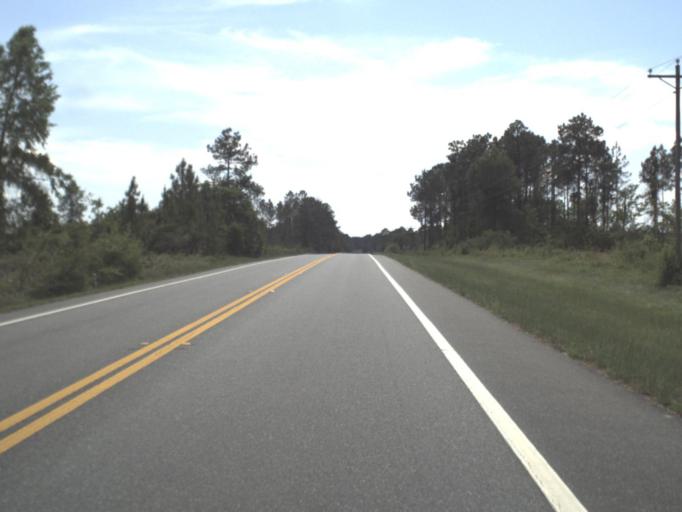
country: US
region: Florida
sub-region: Gulf County
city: Wewahitchka
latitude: 30.2523
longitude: -85.2028
